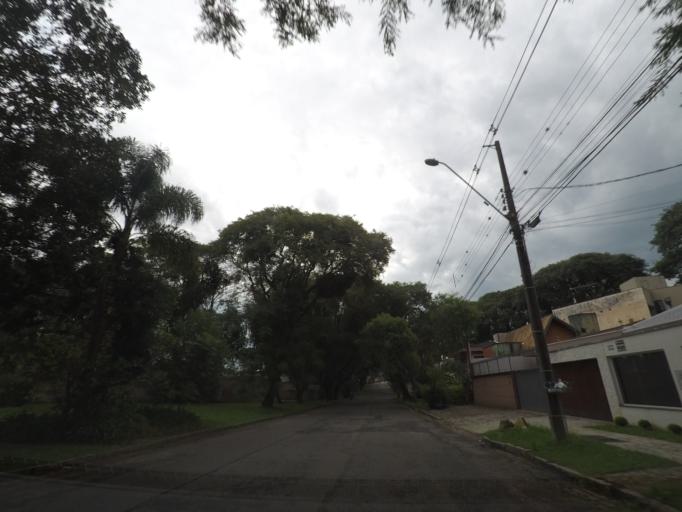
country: BR
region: Parana
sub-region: Curitiba
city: Curitiba
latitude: -25.4512
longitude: -49.3083
